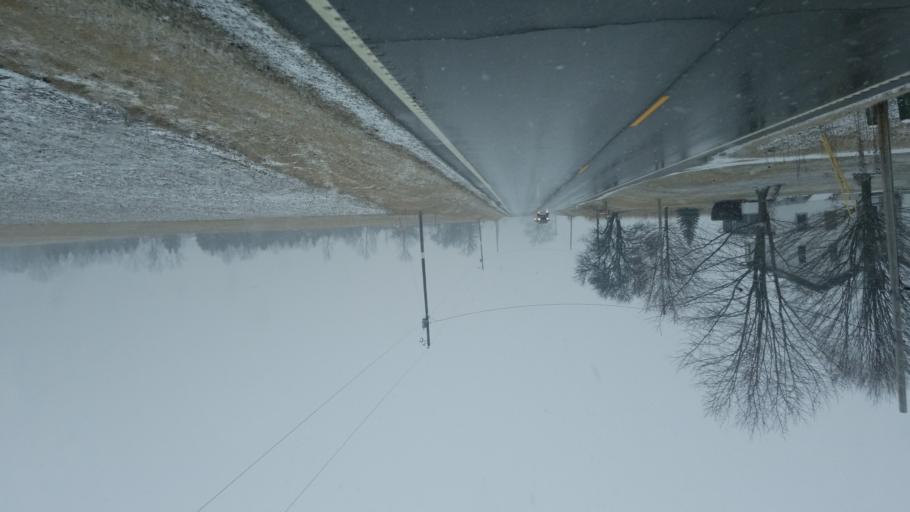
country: US
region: Ohio
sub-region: Defiance County
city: Hicksville
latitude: 41.3351
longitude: -84.7478
